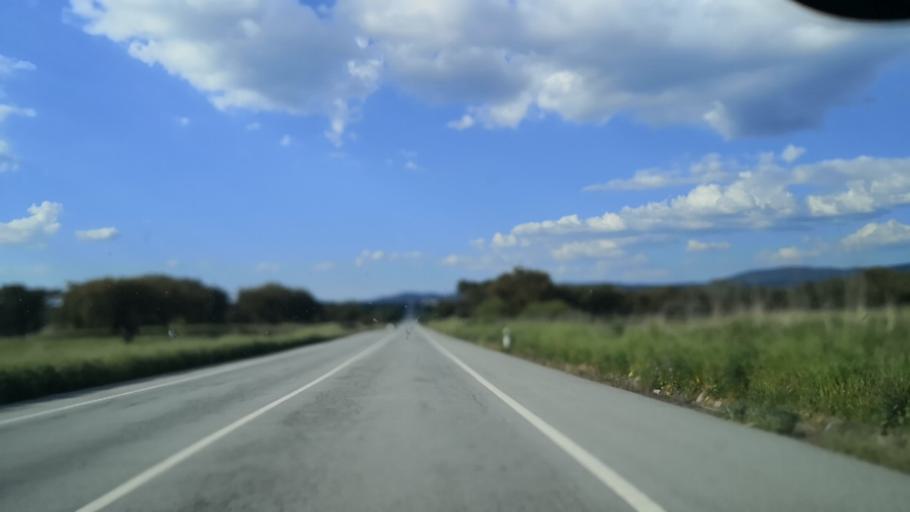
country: PT
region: Portalegre
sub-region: Portalegre
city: Urra
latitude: 39.2260
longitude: -7.4558
